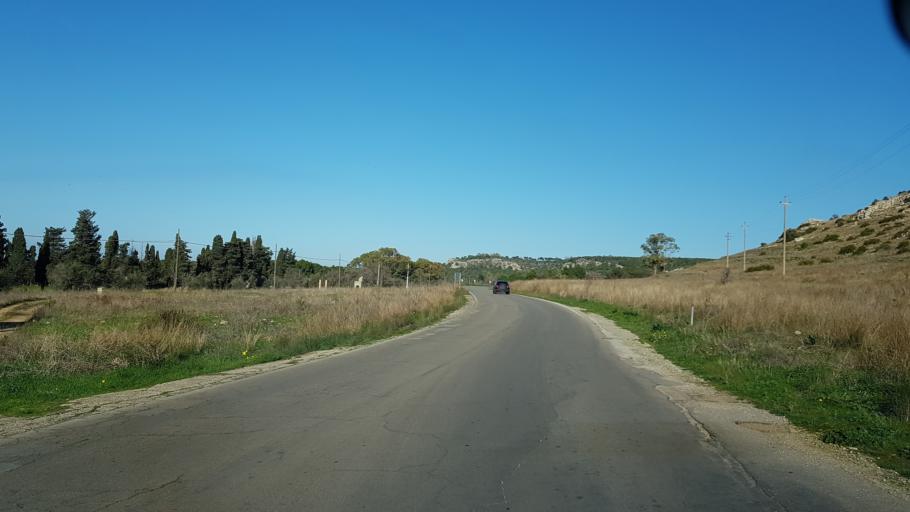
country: IT
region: Apulia
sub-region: Provincia di Lecce
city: Sannicola
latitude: 40.0973
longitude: 18.0210
